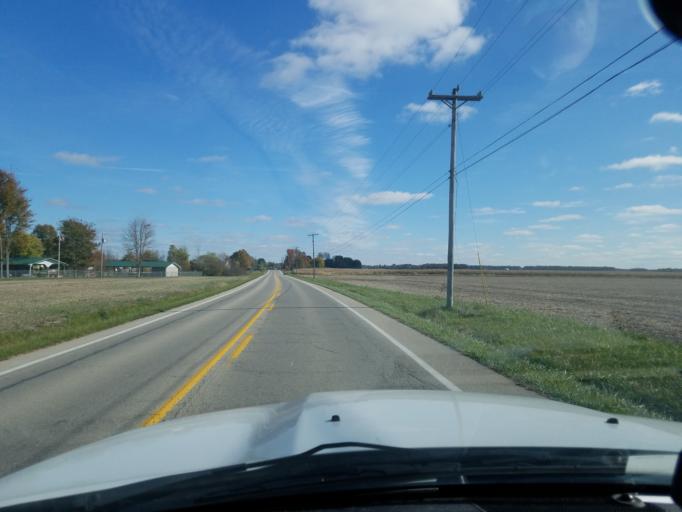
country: US
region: Indiana
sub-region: Ripley County
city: Osgood
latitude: 39.0731
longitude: -85.3845
